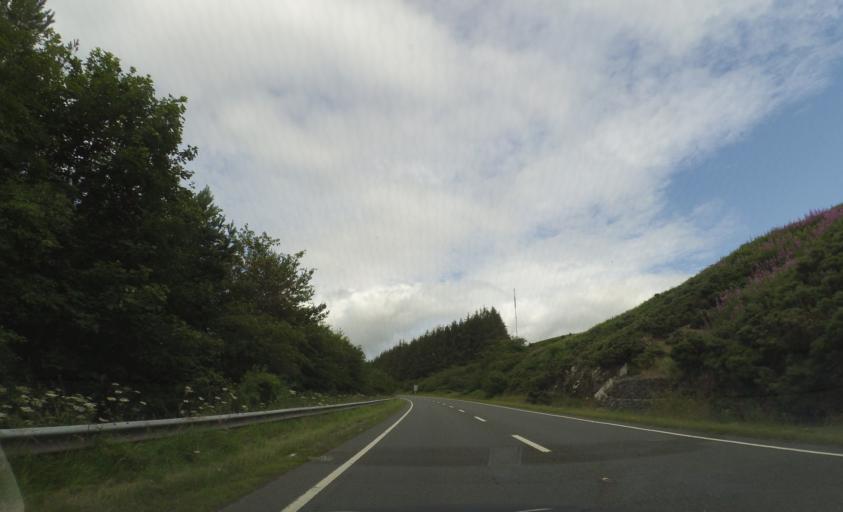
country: GB
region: Scotland
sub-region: The Scottish Borders
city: Selkirk
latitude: 55.5029
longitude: -2.8338
